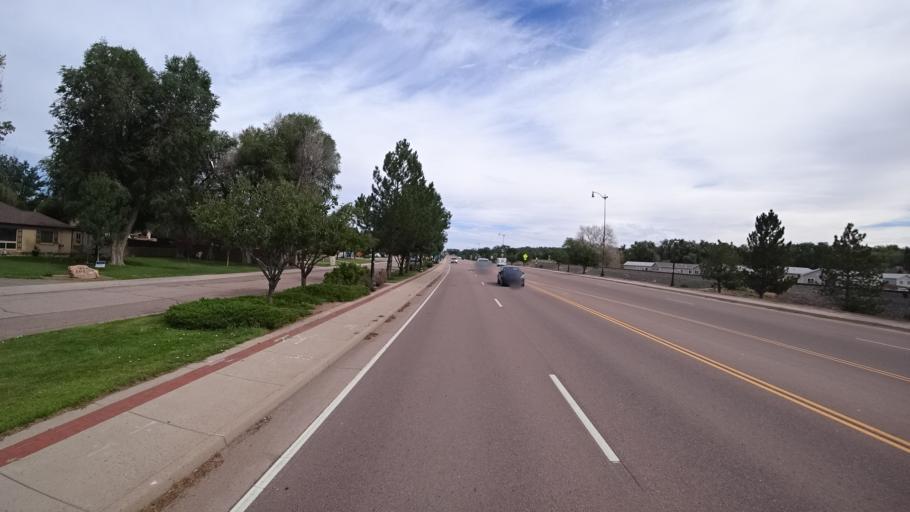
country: US
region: Colorado
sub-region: El Paso County
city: Fountain
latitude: 38.6901
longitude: -104.7047
